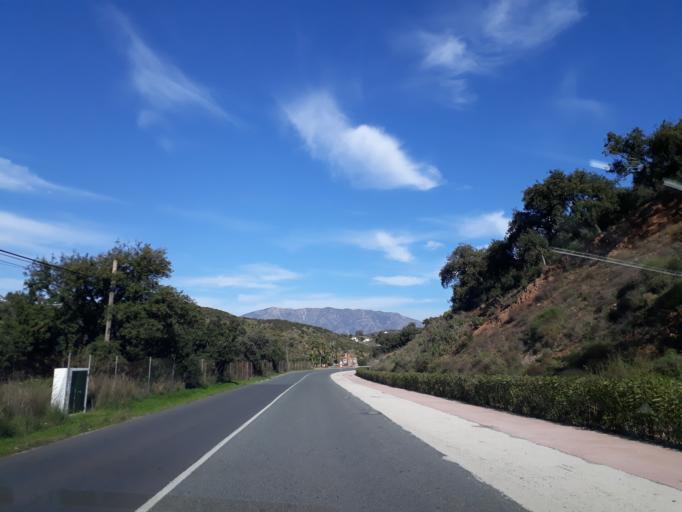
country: ES
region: Andalusia
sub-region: Provincia de Malaga
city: Fuengirola
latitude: 36.5131
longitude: -4.6871
